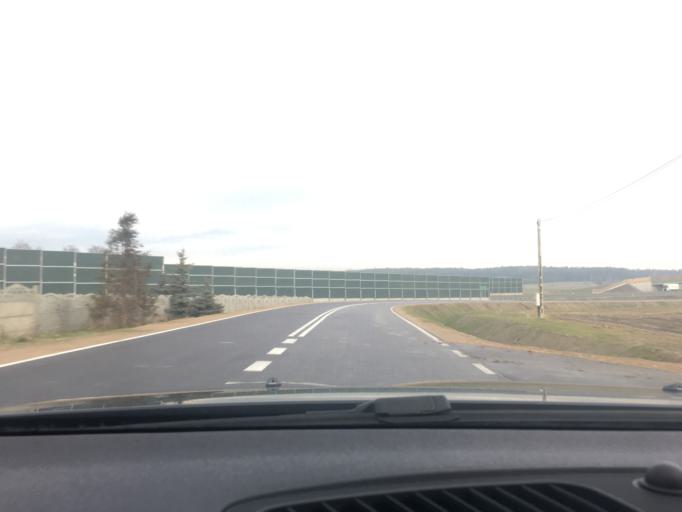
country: PL
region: Swietokrzyskie
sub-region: Powiat jedrzejowski
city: Jedrzejow
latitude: 50.6608
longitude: 20.3329
